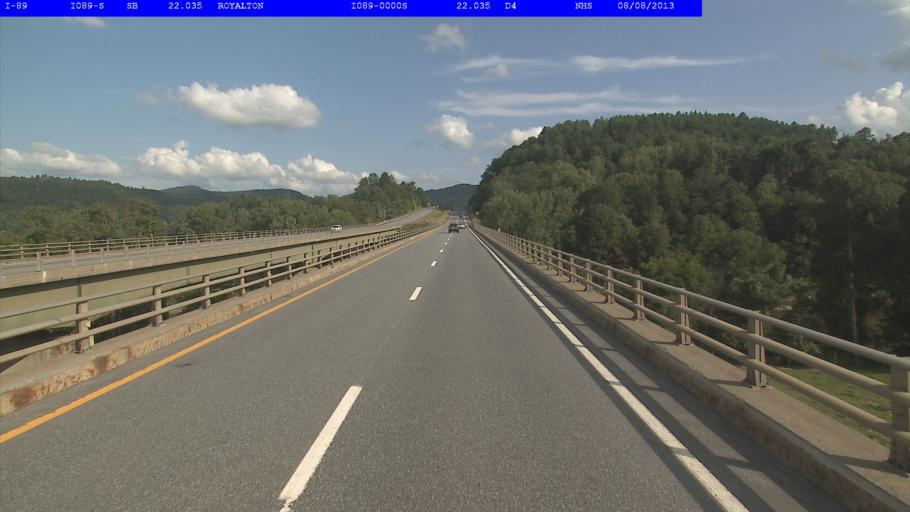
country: US
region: Vermont
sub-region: Orange County
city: Randolph
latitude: 43.8259
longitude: -72.5787
